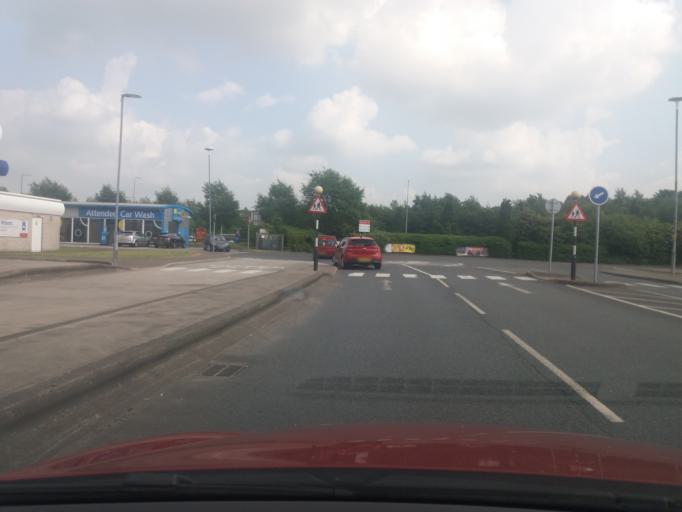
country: GB
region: England
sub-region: Borough of Bolton
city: Horwich
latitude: 53.5816
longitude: -2.5294
